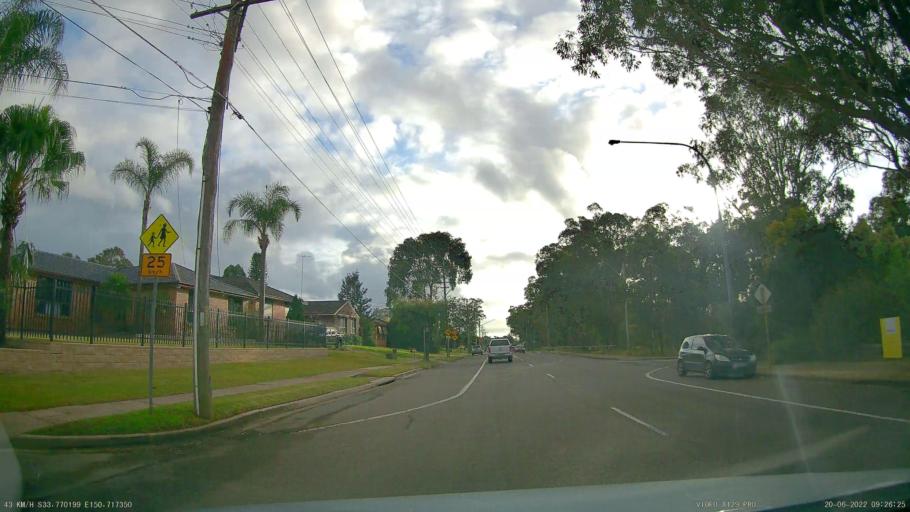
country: AU
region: New South Wales
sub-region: Penrith Municipality
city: Kingswood Park
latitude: -33.7700
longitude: 150.7174
